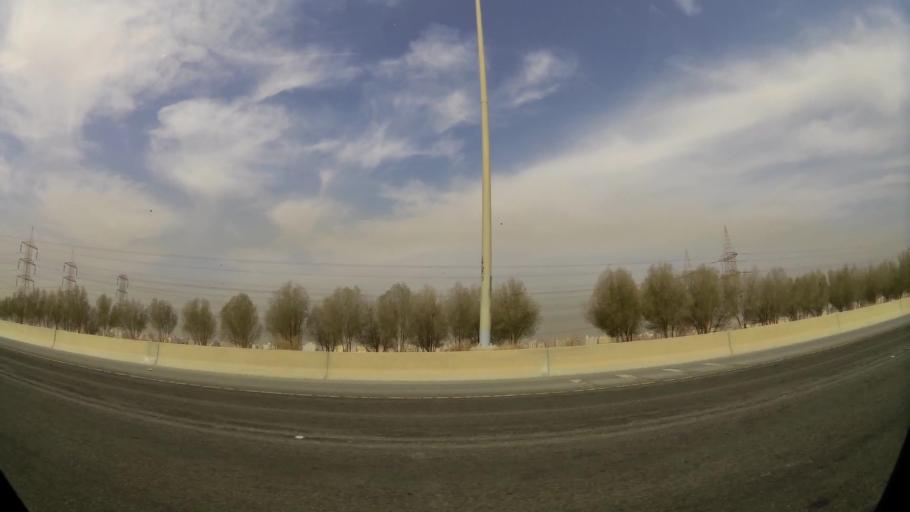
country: KW
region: Muhafazat al Jahra'
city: Al Jahra'
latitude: 29.3274
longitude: 47.7873
